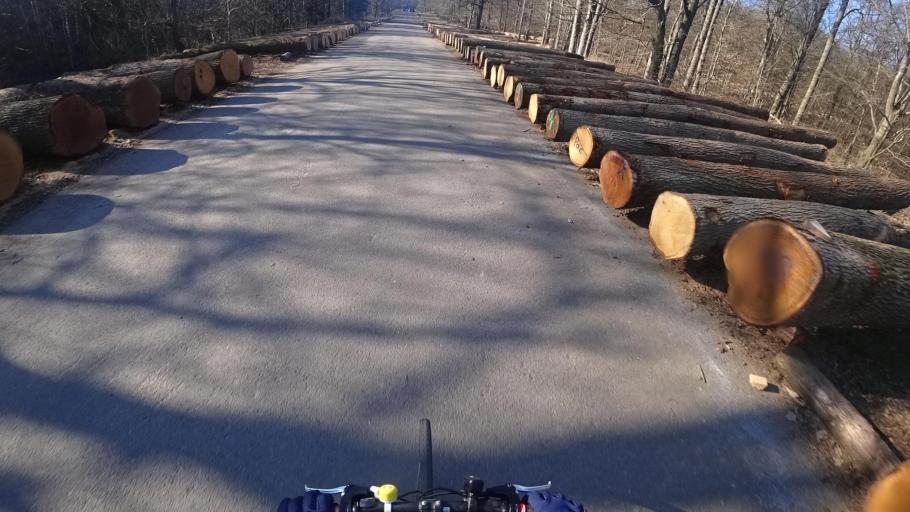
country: DE
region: Rheinland-Pfalz
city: Nortershausen
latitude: 50.2275
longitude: 7.5234
